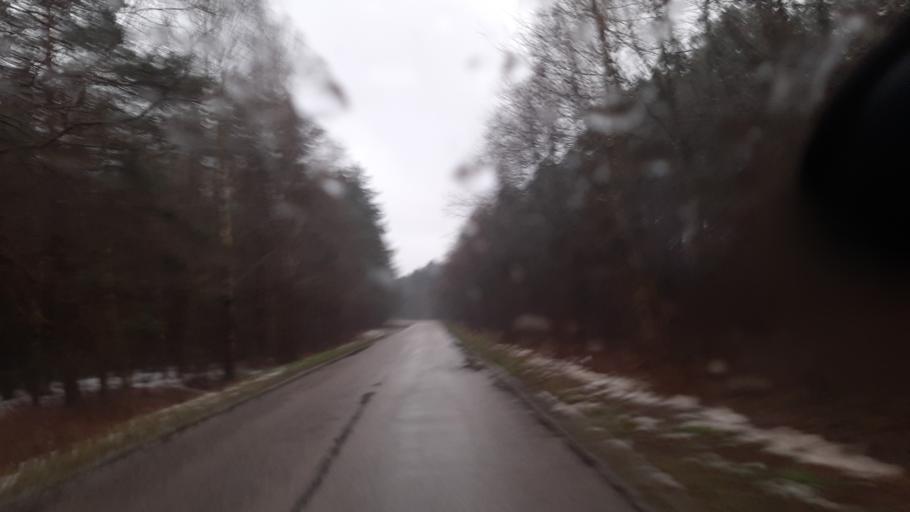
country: PL
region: Lublin Voivodeship
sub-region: Powiat lubartowski
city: Firlej
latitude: 51.5123
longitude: 22.4925
